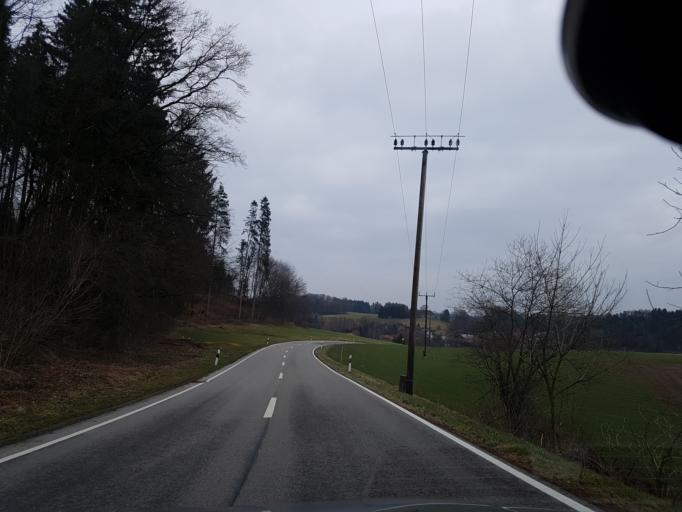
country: DE
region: Bavaria
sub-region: Upper Bavaria
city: Feldkirchen-Westerham
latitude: 47.9402
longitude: 11.8536
